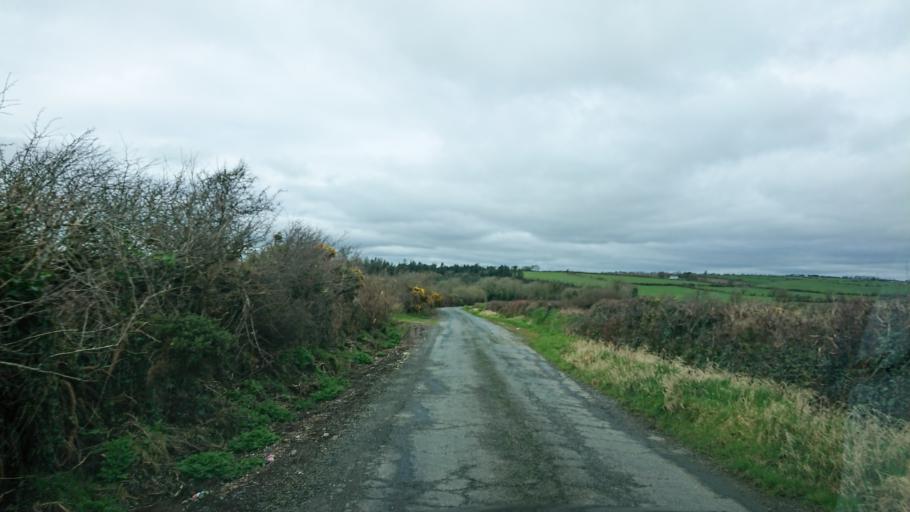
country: IE
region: Munster
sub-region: Waterford
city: Dunmore East
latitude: 52.1646
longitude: -7.0373
